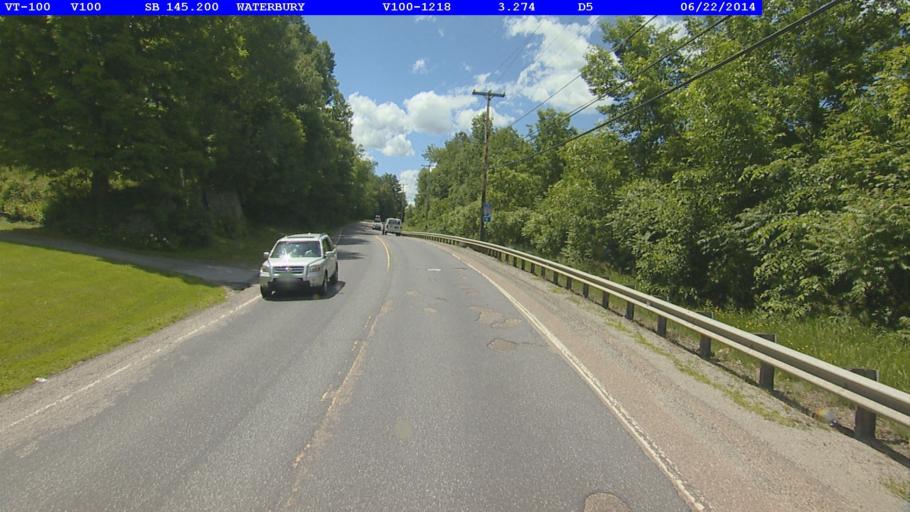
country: US
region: Vermont
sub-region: Washington County
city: Waterbury
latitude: 44.3775
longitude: -72.7248
